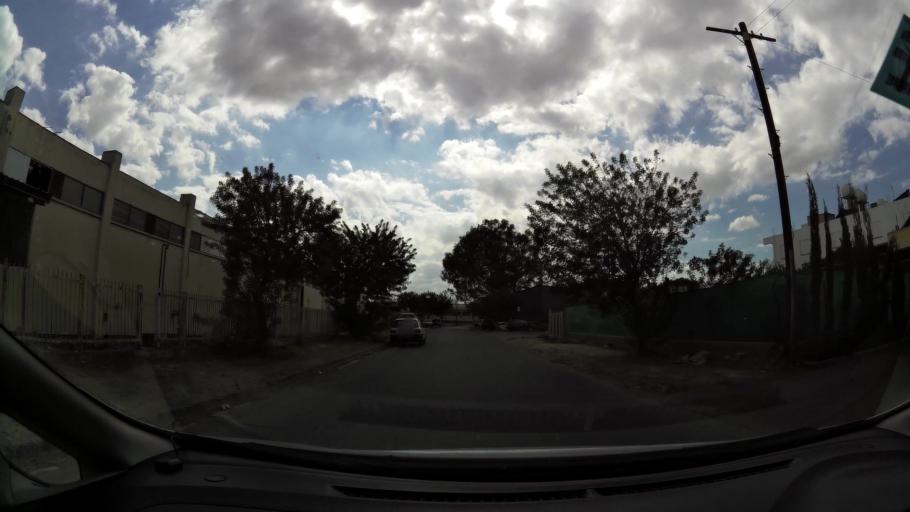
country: CY
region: Lefkosia
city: Nicosia
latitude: 35.1801
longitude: 33.3908
